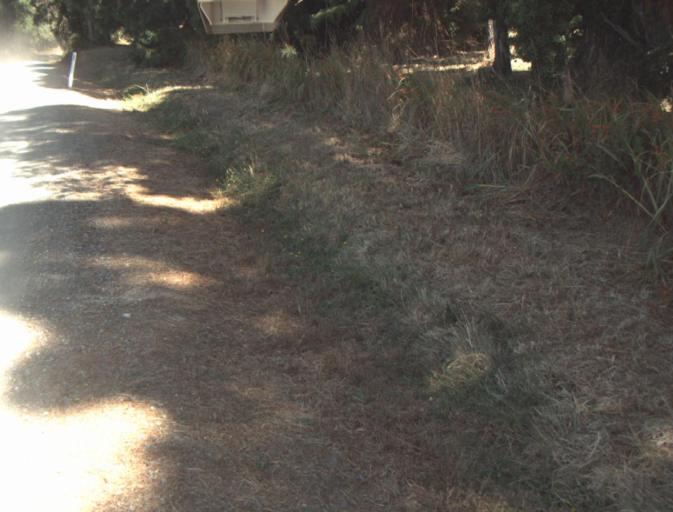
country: AU
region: Tasmania
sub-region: Launceston
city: Mayfield
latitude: -41.2569
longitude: 147.1734
